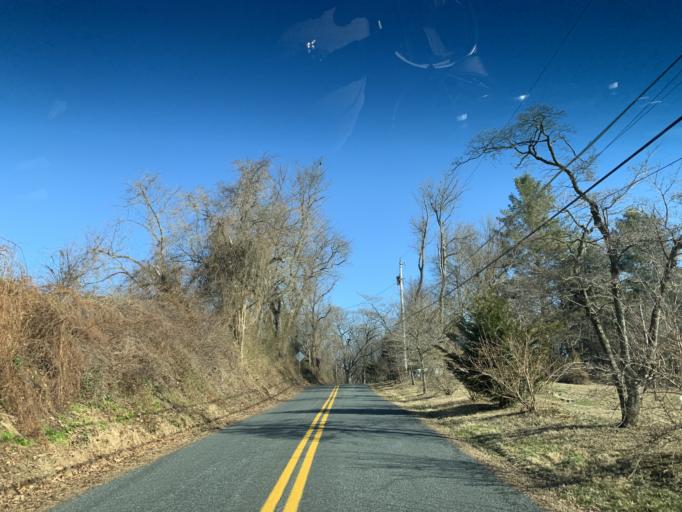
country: US
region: Maryland
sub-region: Harford County
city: Aberdeen
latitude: 39.6052
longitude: -76.2241
